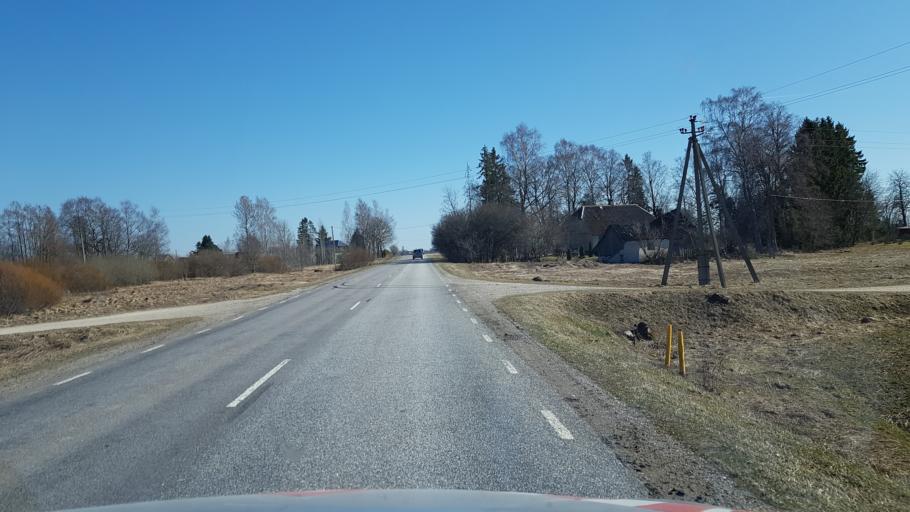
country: EE
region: Laeaene-Virumaa
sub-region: Vaeike-Maarja vald
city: Vaike-Maarja
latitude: 59.1465
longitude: 26.2287
